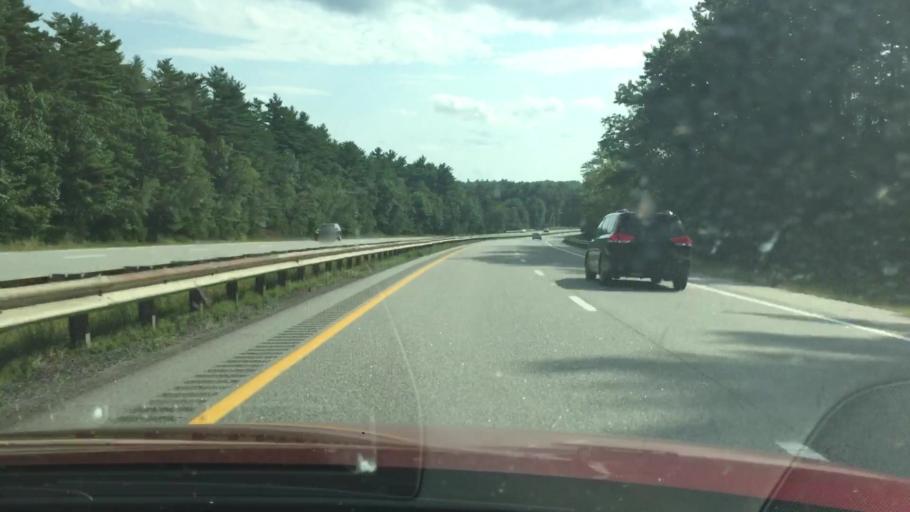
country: US
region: Maine
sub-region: Cumberland County
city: New Gloucester
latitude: 43.9821
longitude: -70.3113
